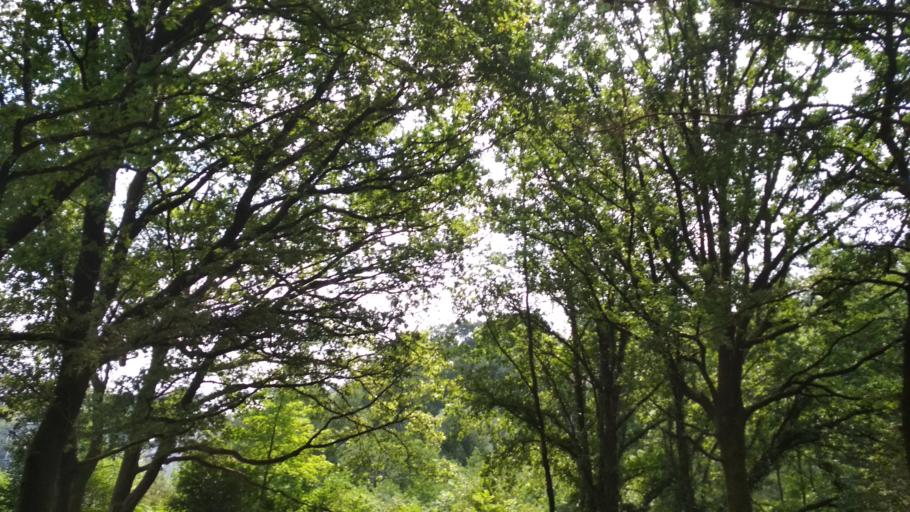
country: ES
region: Basque Country
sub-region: Provincia de Guipuzcoa
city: San Sebastian
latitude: 43.2971
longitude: -1.9776
